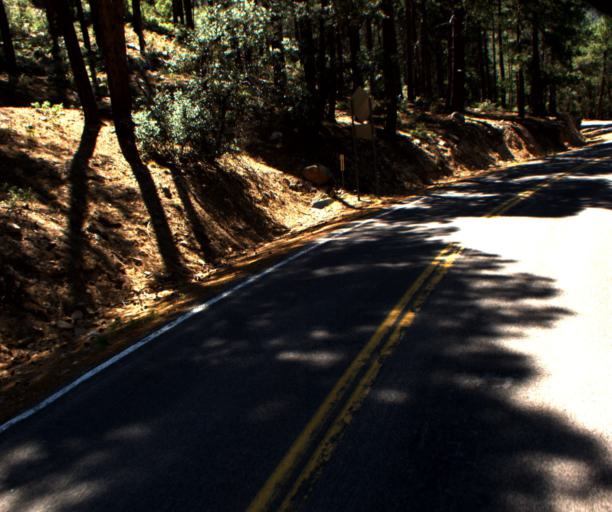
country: US
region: Arizona
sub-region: Graham County
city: Swift Trail Junction
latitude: 32.6475
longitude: -109.8177
